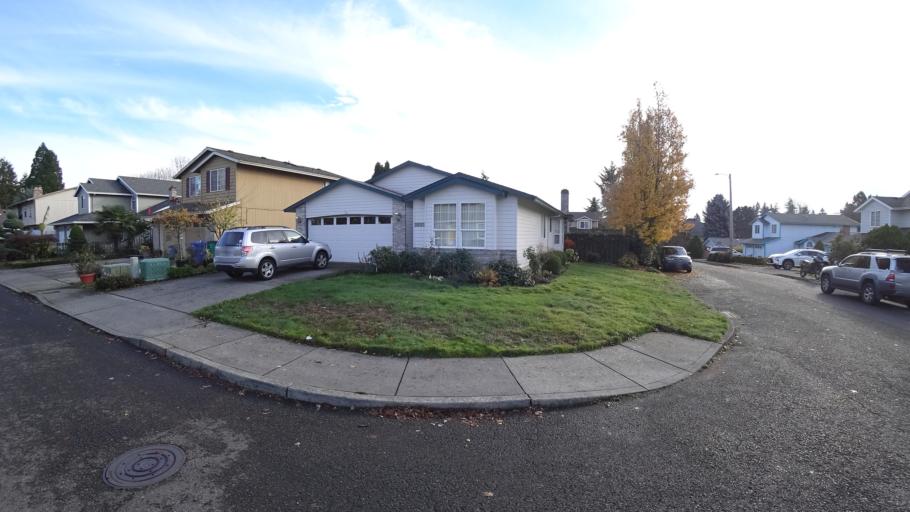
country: US
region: Oregon
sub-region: Multnomah County
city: Lents
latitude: 45.5243
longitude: -122.5248
